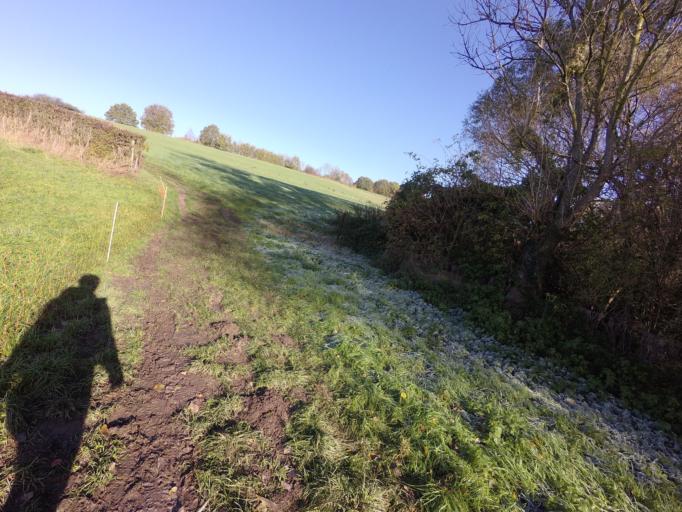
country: NL
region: Limburg
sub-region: Valkenburg aan de Geul
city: Schin op Geul
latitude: 50.8243
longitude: 5.9082
